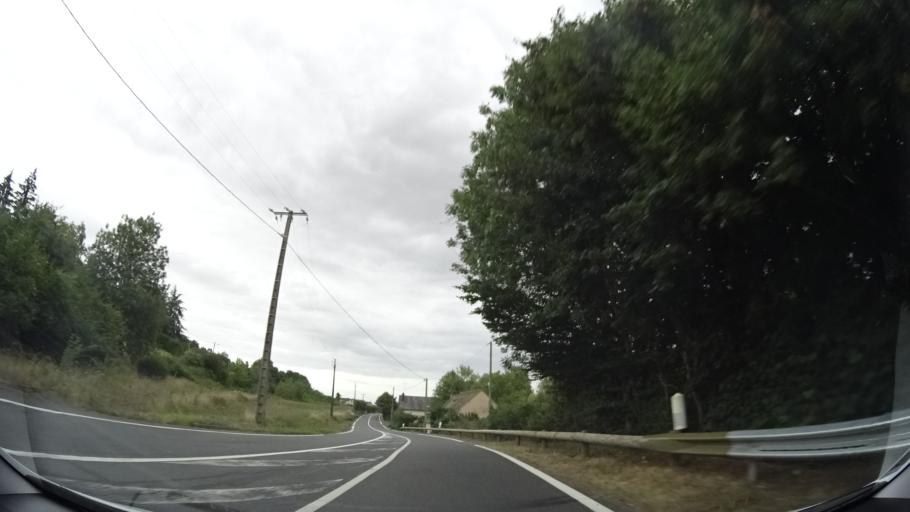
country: FR
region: Centre
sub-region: Departement du Loiret
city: Trigueres
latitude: 47.9392
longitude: 2.9720
